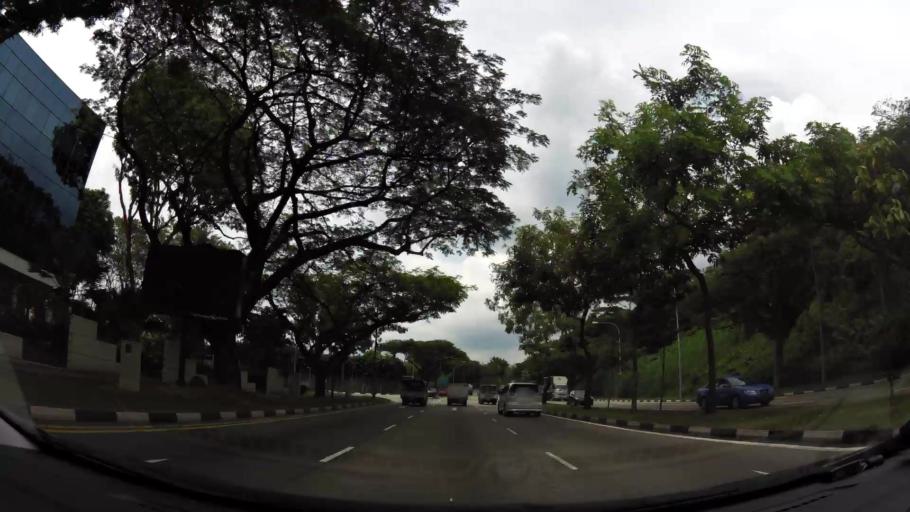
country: SG
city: Singapore
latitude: 1.3280
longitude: 103.7640
